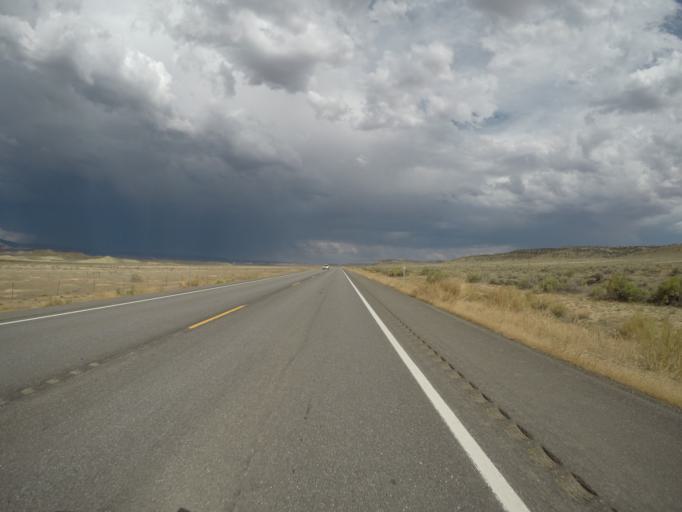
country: US
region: Utah
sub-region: Uintah County
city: Naples
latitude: 40.3001
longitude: -109.1934
